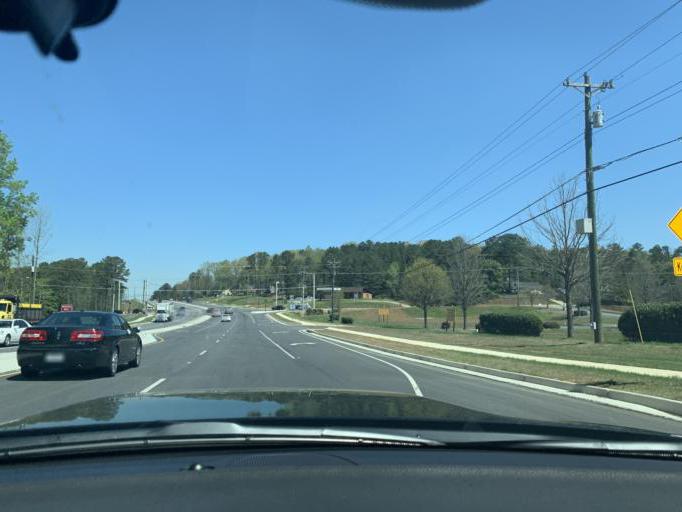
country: US
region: Georgia
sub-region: Forsyth County
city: Cumming
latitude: 34.1990
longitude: -84.1969
